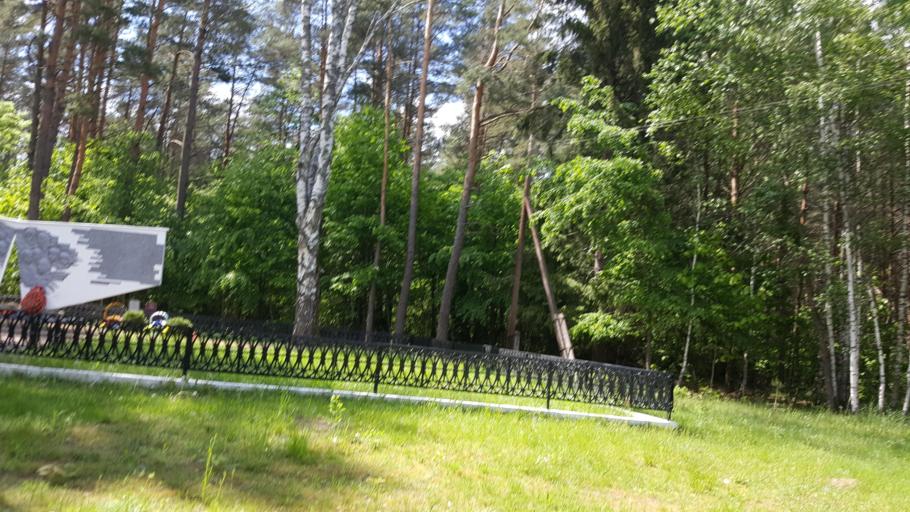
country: BY
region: Brest
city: Kamyanyets
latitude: 52.4511
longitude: 24.0119
